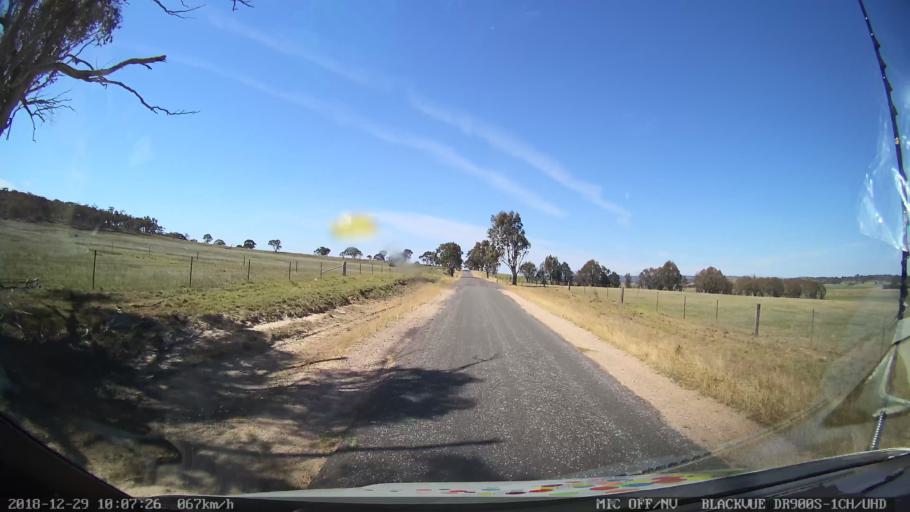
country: AU
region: New South Wales
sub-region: Yass Valley
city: Gundaroo
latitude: -34.8528
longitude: 149.4530
